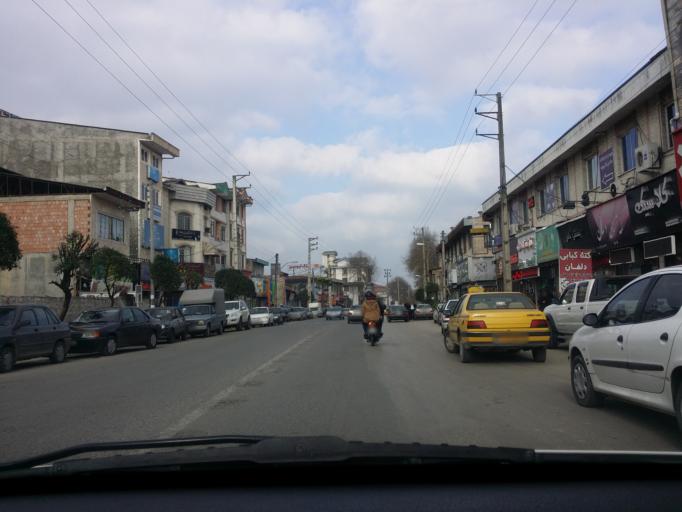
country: IR
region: Mazandaran
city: Chalus
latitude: 36.6588
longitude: 51.4145
